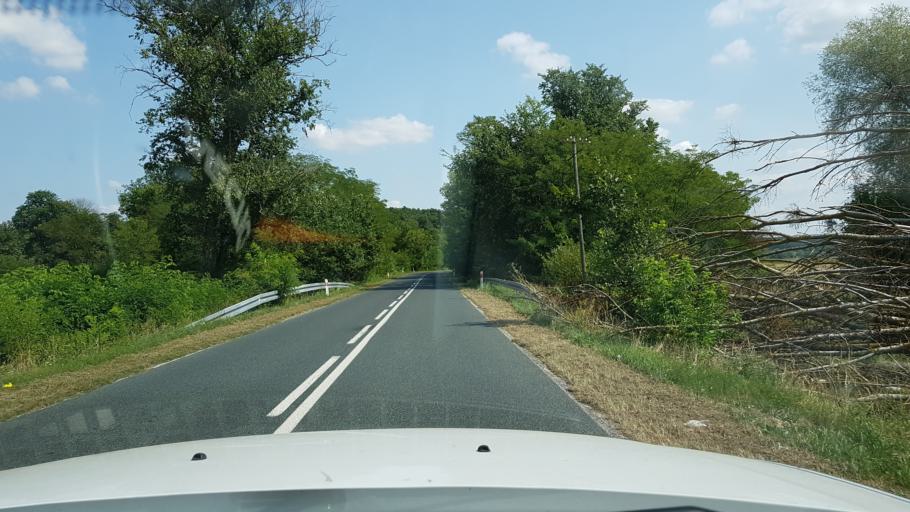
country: PL
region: West Pomeranian Voivodeship
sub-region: Powiat gryfinski
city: Cedynia
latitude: 52.8338
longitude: 14.1981
